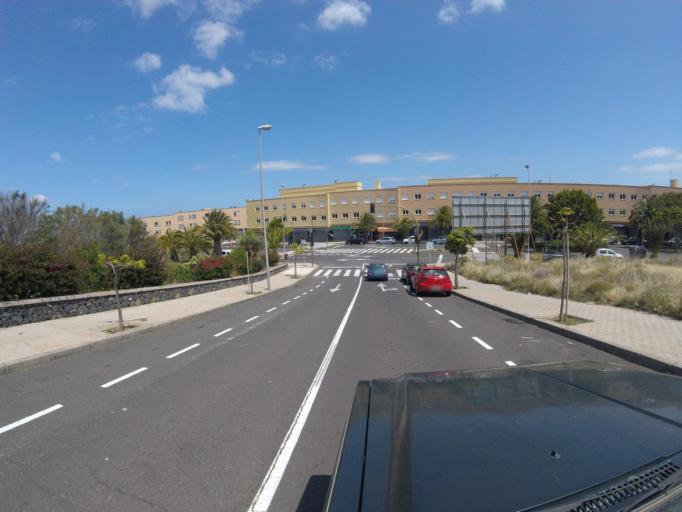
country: ES
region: Canary Islands
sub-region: Provincia de Santa Cruz de Tenerife
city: La Laguna
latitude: 28.4437
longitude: -16.3118
